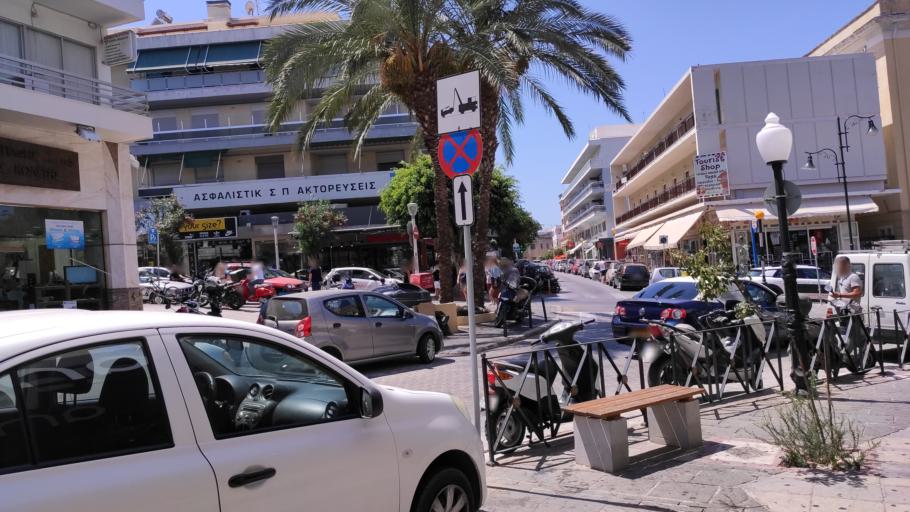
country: GR
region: South Aegean
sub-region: Nomos Dodekanisou
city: Rodos
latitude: 36.4491
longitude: 28.2219
